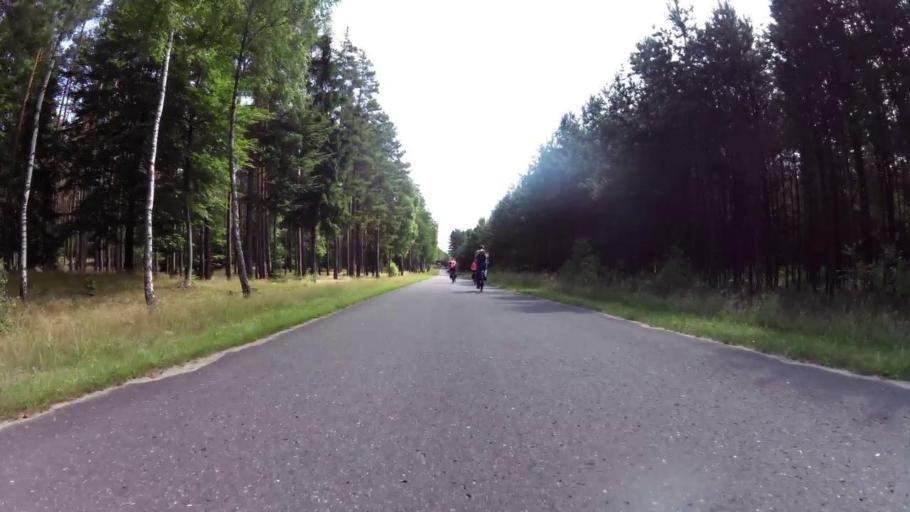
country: PL
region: West Pomeranian Voivodeship
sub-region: Powiat choszczenski
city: Drawno
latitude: 53.3494
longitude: 15.7030
